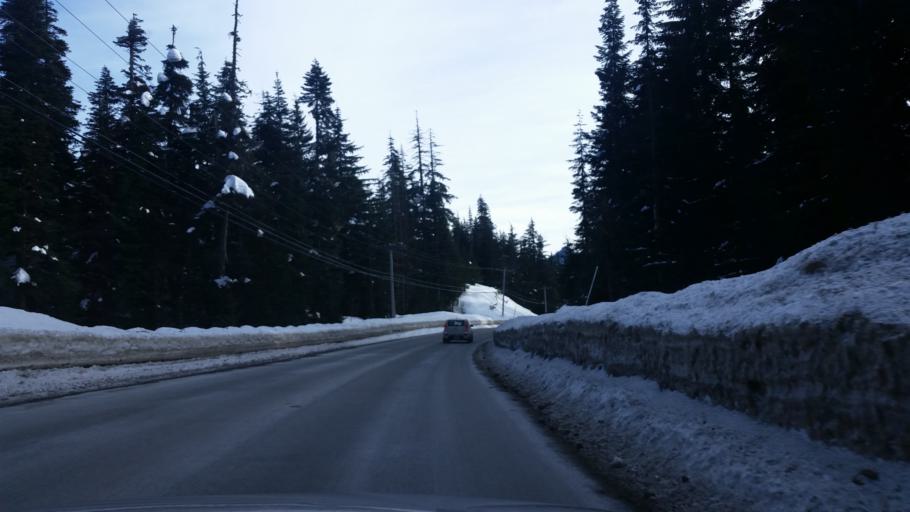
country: US
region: Washington
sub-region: King County
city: Tanner
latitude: 47.4039
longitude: -121.4084
